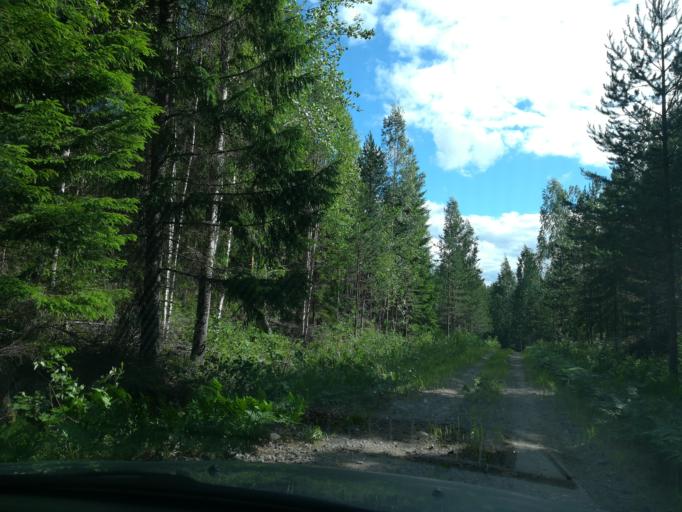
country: FI
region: South Karelia
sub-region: Lappeenranta
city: Savitaipale
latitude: 61.3006
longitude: 27.6174
